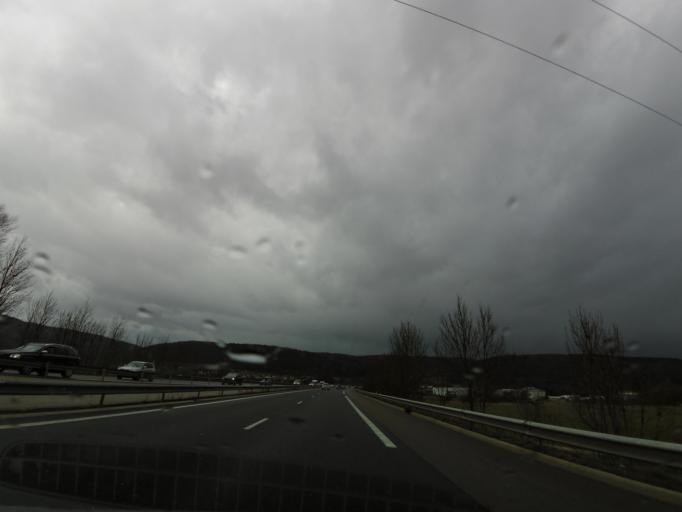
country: FR
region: Rhone-Alpes
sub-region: Departement de l'Ain
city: Saint-Martin-du-Frene
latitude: 46.1291
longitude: 5.5529
